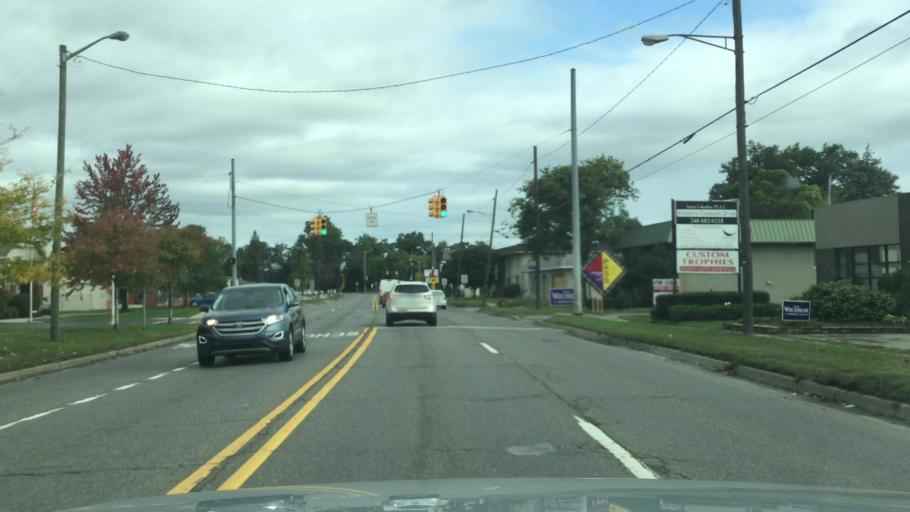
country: US
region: Michigan
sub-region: Oakland County
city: Keego Harbor
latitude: 42.6014
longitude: -83.3487
